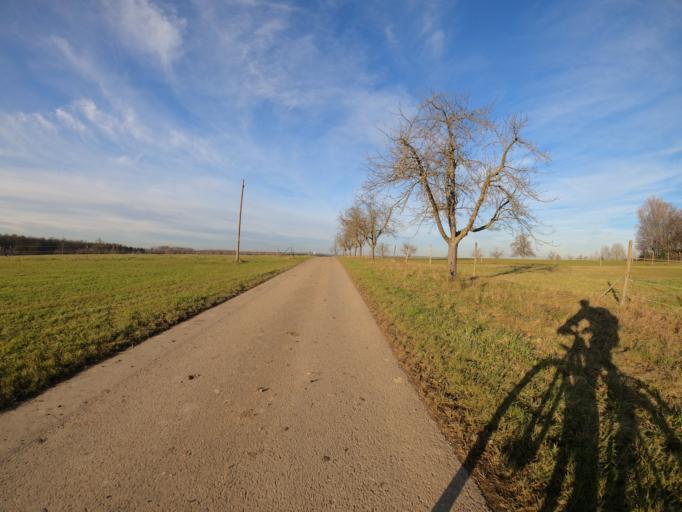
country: DE
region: Baden-Wuerttemberg
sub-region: Regierungsbezirk Stuttgart
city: Hattenhofen
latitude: 48.6692
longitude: 9.5539
